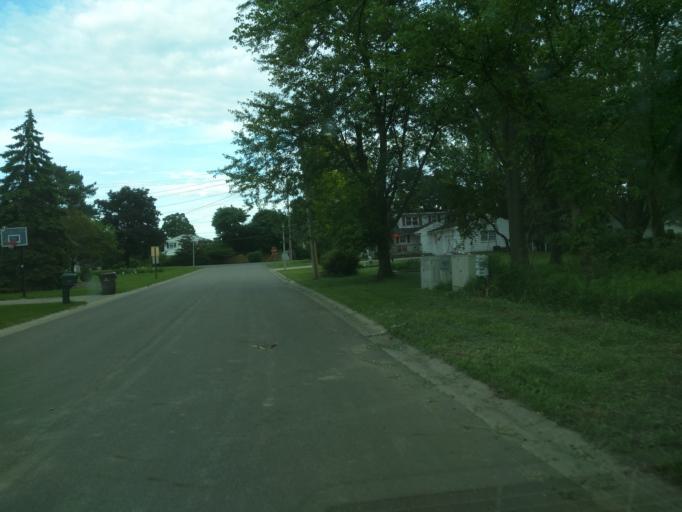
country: US
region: Michigan
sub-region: Eaton County
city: Waverly
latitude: 42.7524
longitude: -84.6139
